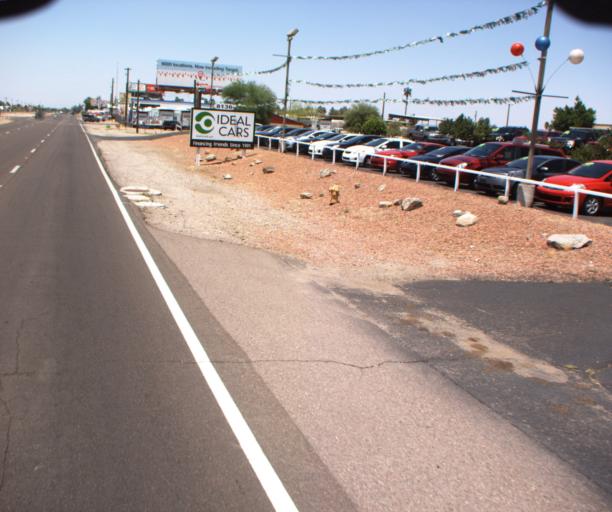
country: US
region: Arizona
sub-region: Pinal County
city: Apache Junction
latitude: 33.4155
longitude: -111.6547
